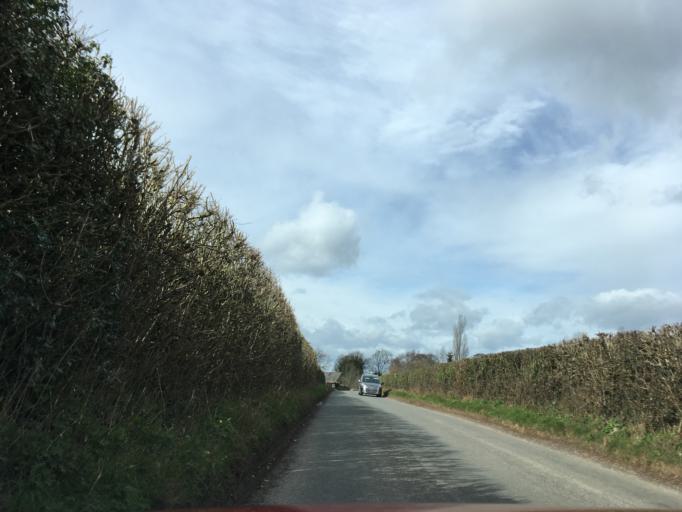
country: GB
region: England
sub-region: Gloucestershire
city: Coleford
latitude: 51.7643
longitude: -2.6189
